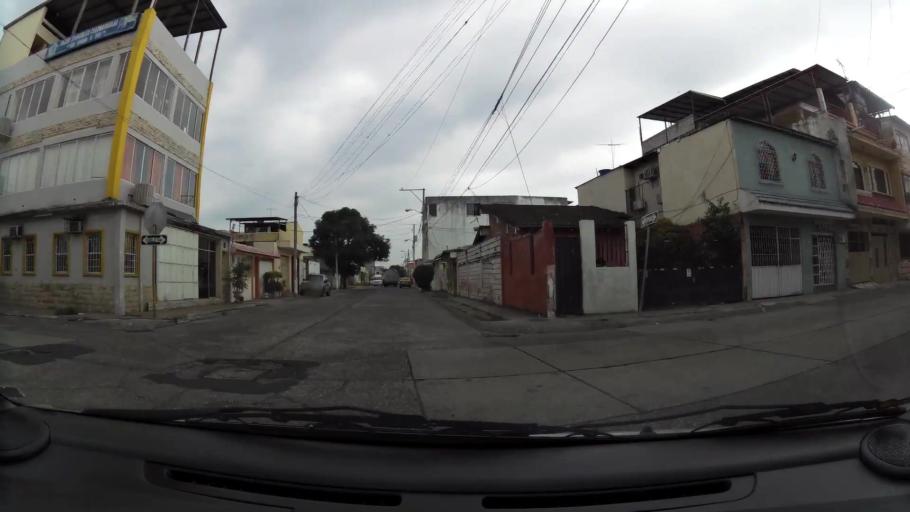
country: EC
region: Guayas
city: Eloy Alfaro
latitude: -2.1213
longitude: -79.8845
